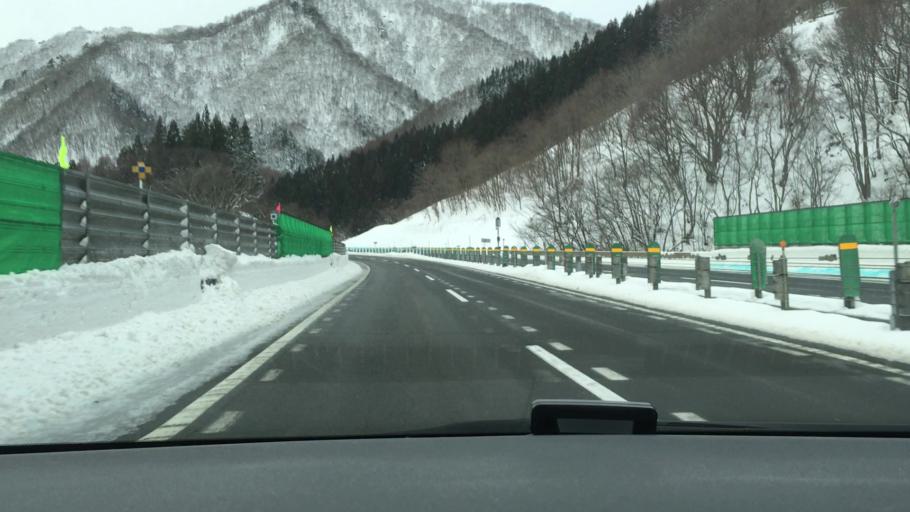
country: JP
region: Akita
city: Hanawa
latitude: 40.1315
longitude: 140.9204
